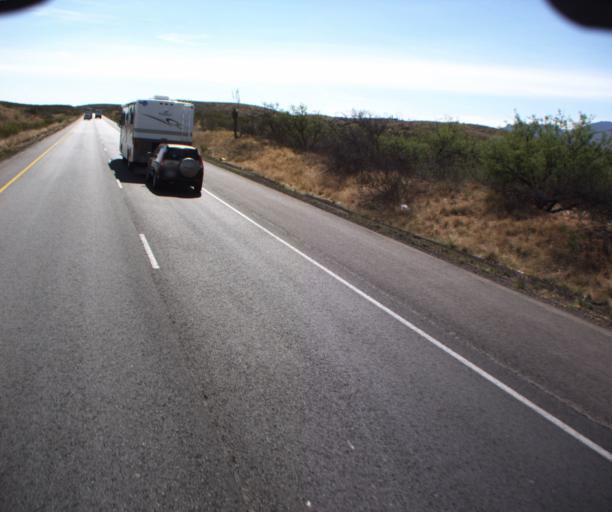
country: US
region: Arizona
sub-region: Cochise County
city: Mescal
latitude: 31.9706
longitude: -110.4859
